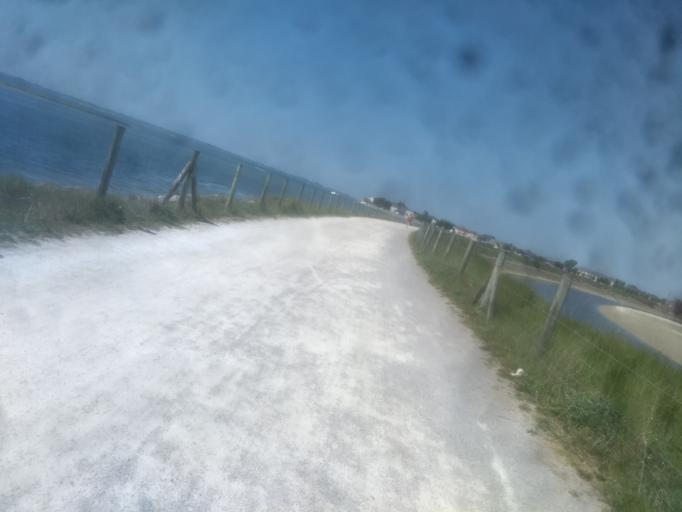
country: FR
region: Picardie
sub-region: Departement de la Somme
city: Le Crotoy
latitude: 50.2130
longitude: 1.6386
